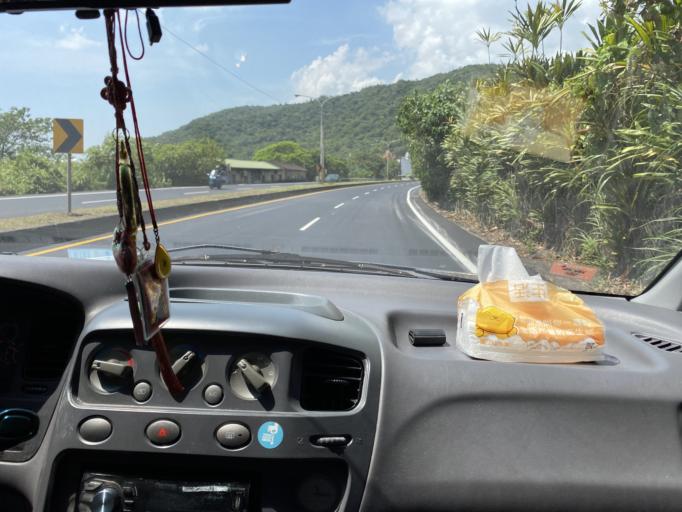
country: TW
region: Taiwan
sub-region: Yilan
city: Yilan
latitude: 24.8925
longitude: 121.8540
